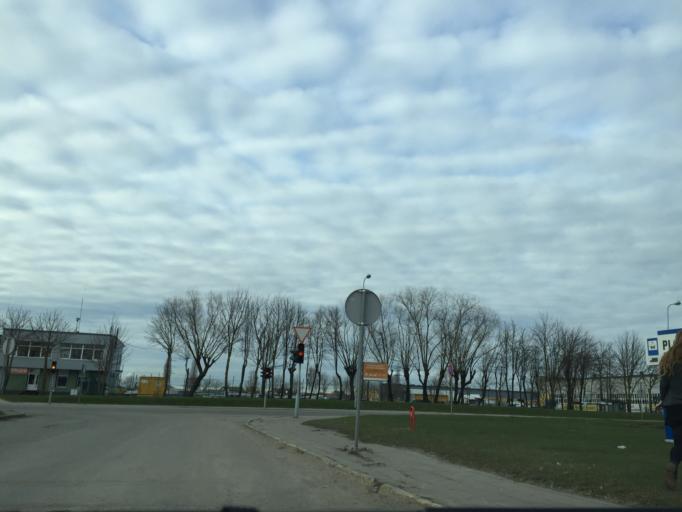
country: LT
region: Klaipedos apskritis
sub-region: Klaipeda
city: Klaipeda
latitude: 55.7052
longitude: 21.1664
